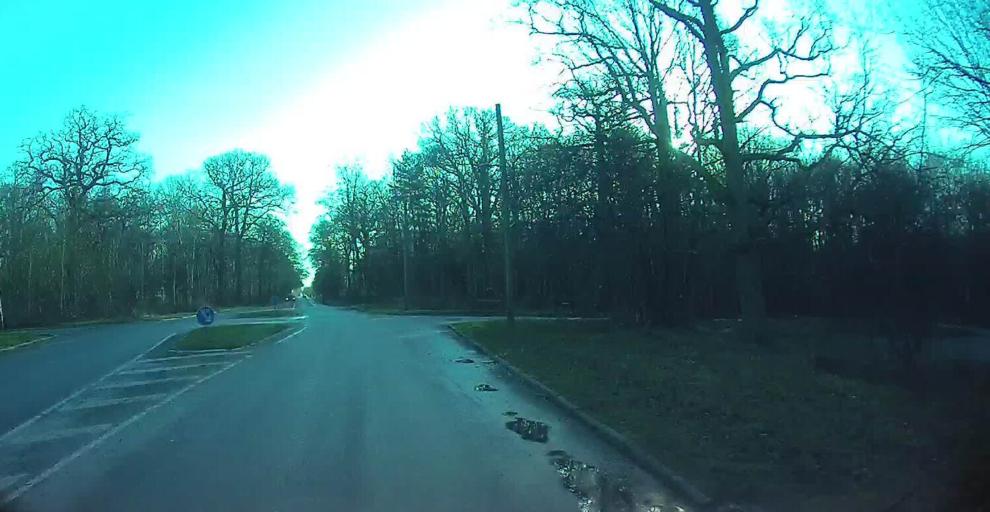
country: DK
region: Capital Region
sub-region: Tarnby Kommune
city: Tarnby
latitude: 55.5754
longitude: 12.5791
